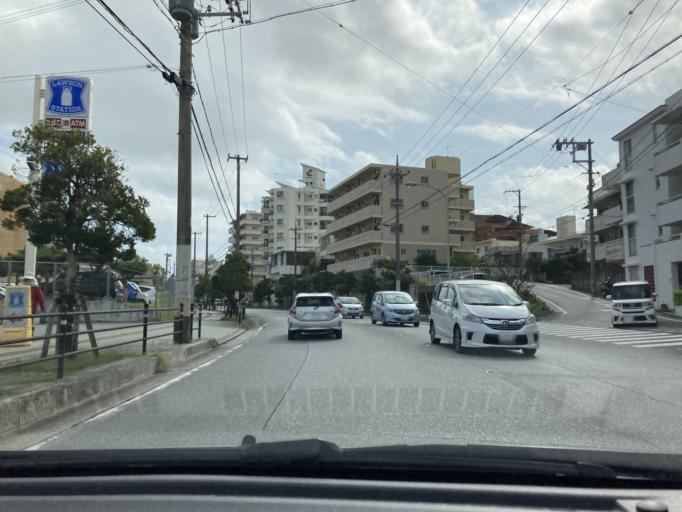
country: JP
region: Okinawa
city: Ginowan
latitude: 26.2615
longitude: 127.7524
